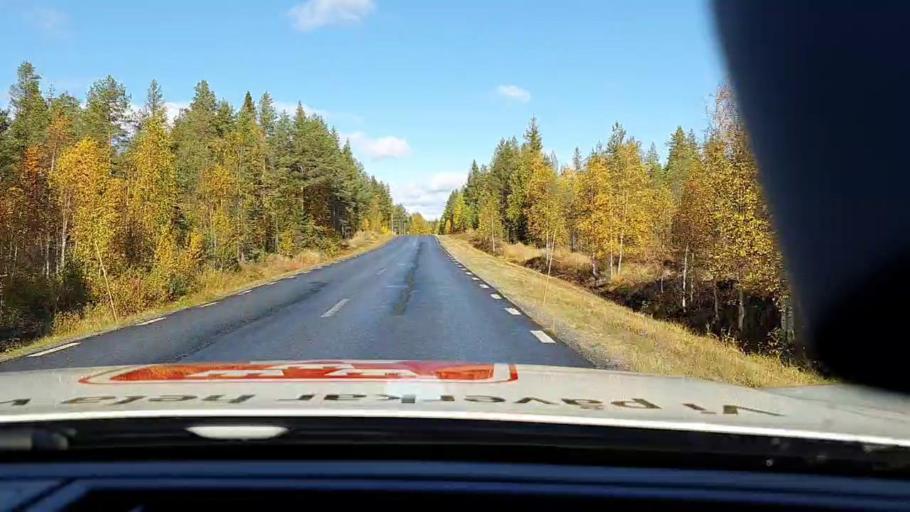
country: SE
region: Vaesterbotten
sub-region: Skelleftea Kommun
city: Langsele
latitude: 64.9964
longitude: 20.0902
